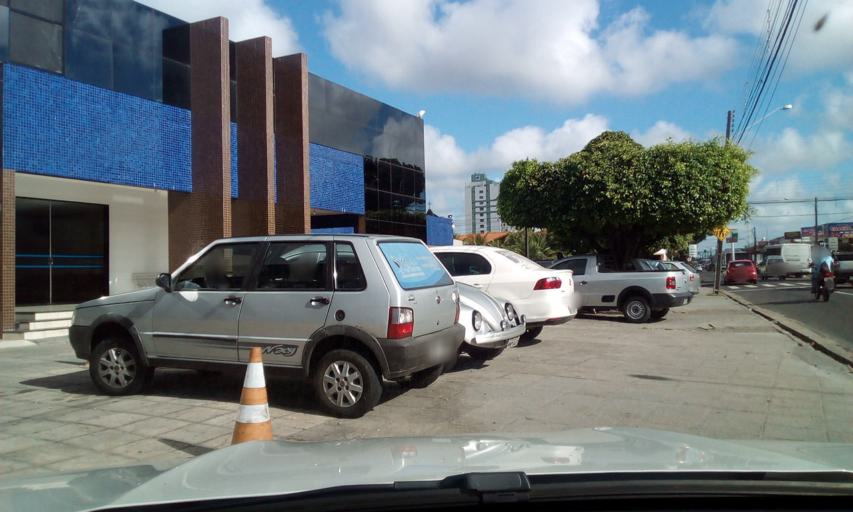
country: BR
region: Paraiba
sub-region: Joao Pessoa
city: Joao Pessoa
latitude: -7.1351
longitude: -34.8789
